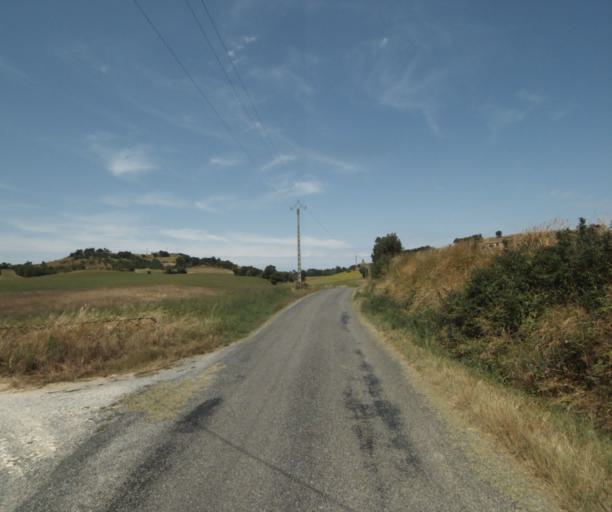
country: FR
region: Midi-Pyrenees
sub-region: Departement de la Haute-Garonne
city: Saint-Felix-Lauragais
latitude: 43.4343
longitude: 1.8947
